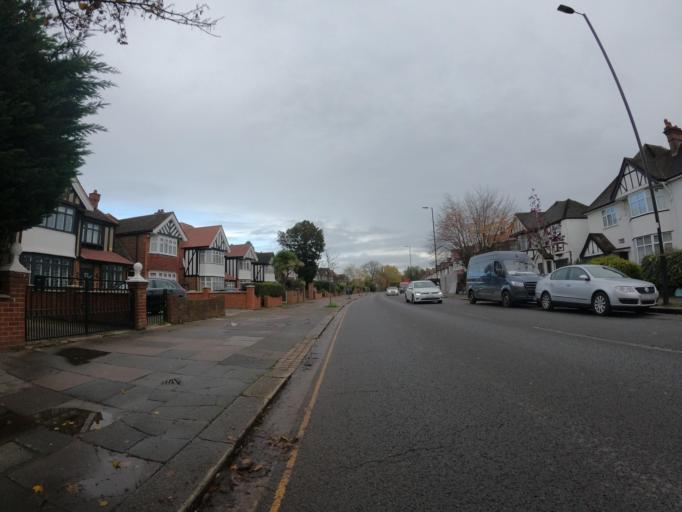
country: GB
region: England
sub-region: Greater London
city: Ealing
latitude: 51.5016
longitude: -0.2921
